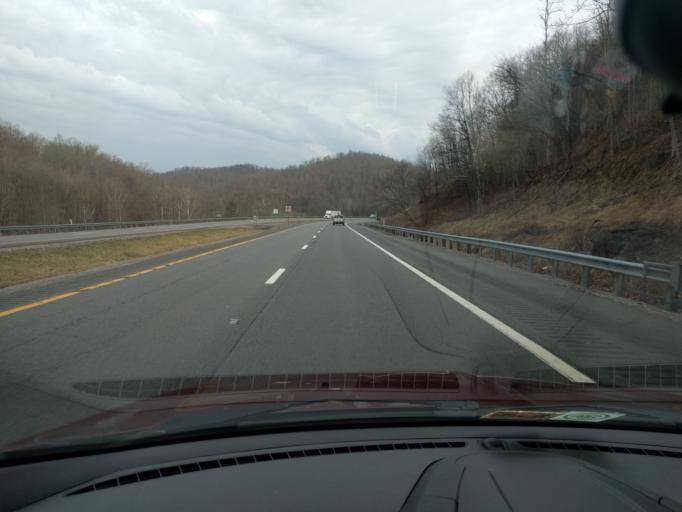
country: US
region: West Virginia
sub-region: Jackson County
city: Ravenswood
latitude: 38.9748
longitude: -81.6922
